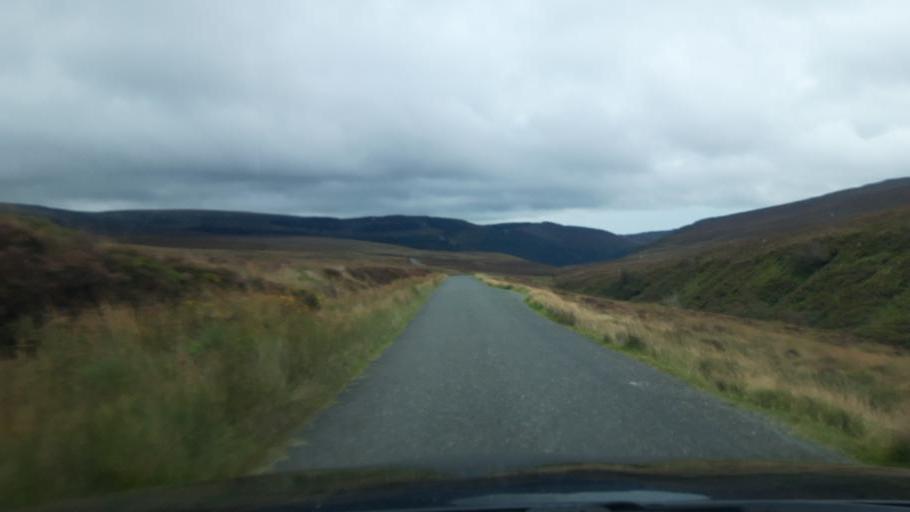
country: IE
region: Leinster
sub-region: Wicklow
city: Enniskerry
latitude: 53.1309
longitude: -6.2971
